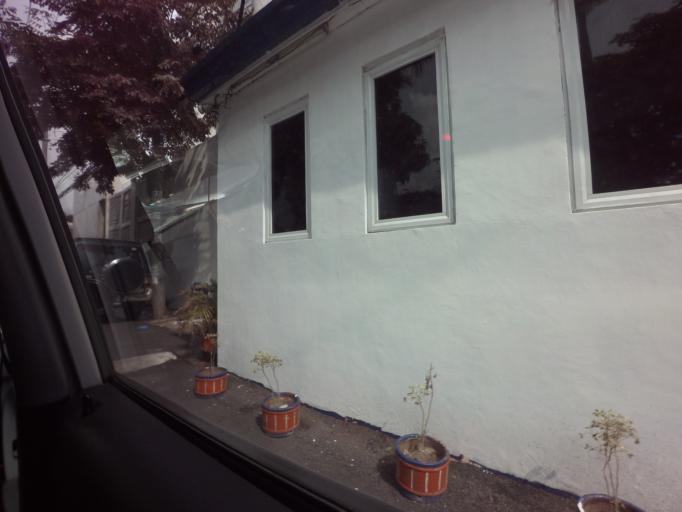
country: PH
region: Metro Manila
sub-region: San Juan
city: San Juan
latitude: 14.6040
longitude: 121.0153
